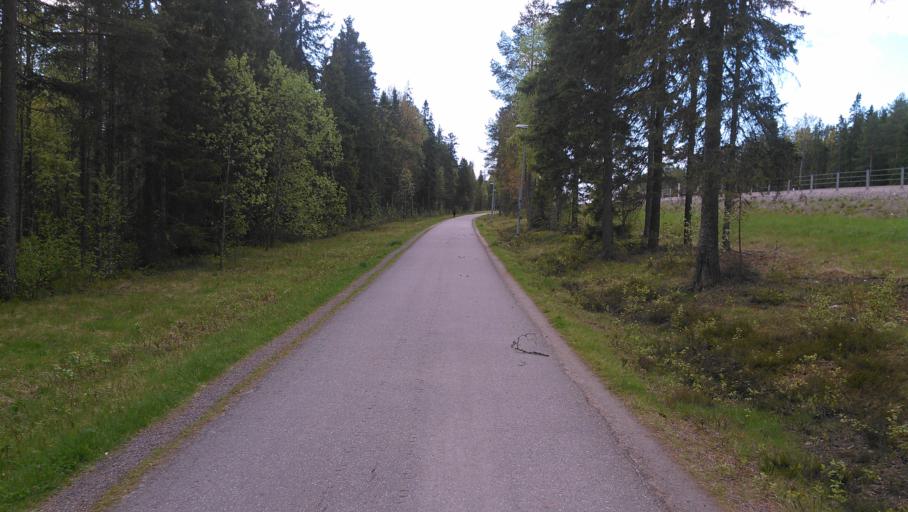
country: SE
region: Vaesterbotten
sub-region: Umea Kommun
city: Ersmark
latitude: 63.8255
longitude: 20.3316
